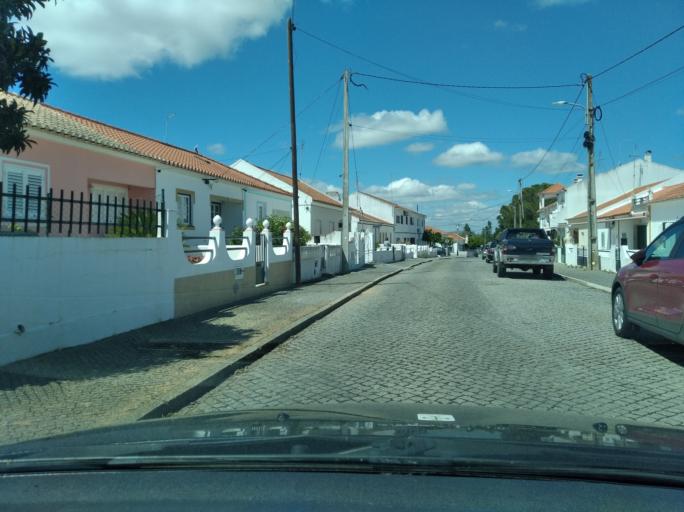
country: PT
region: Portalegre
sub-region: Avis
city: Avis
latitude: 39.0519
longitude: -7.8901
